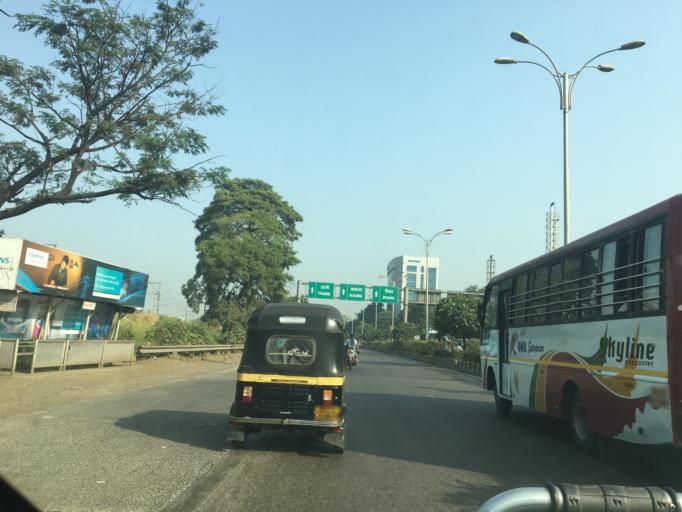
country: IN
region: Maharashtra
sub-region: Thane
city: Airoli
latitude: 19.1508
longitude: 73.0006
